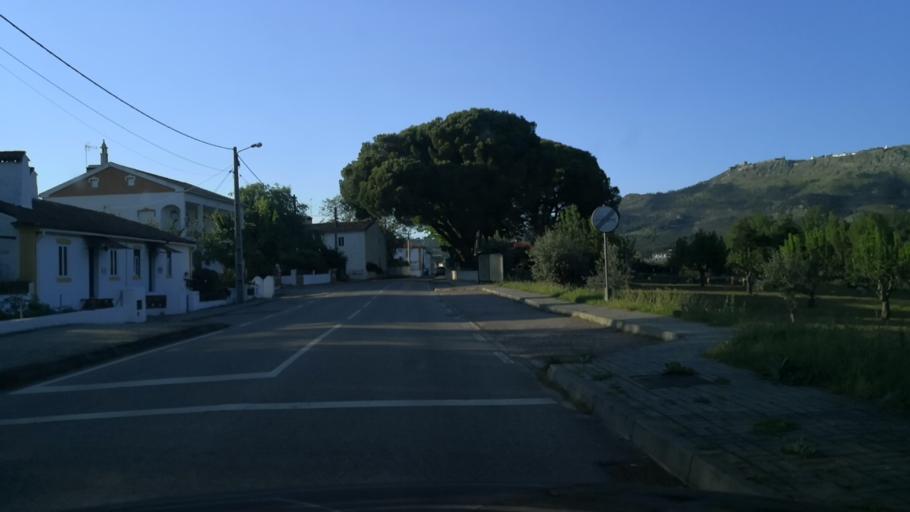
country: PT
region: Portalegre
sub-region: Marvao
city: Marvao
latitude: 39.3729
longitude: -7.3885
